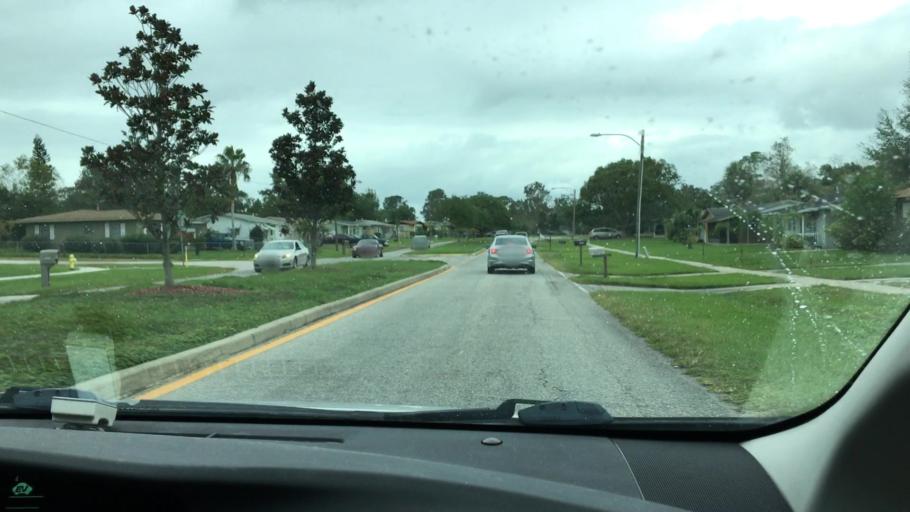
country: US
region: Florida
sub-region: Volusia County
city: Deltona
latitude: 28.8946
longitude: -81.2306
